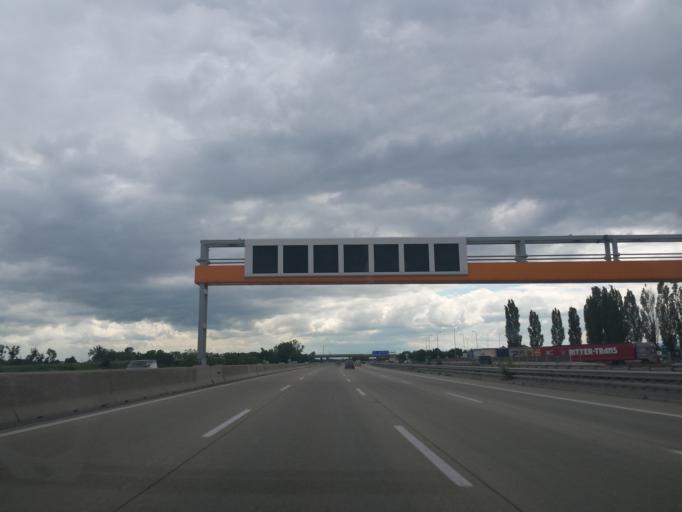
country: AT
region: Lower Austria
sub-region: Politischer Bezirk Modling
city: Guntramsdorf
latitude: 48.0339
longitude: 16.3391
